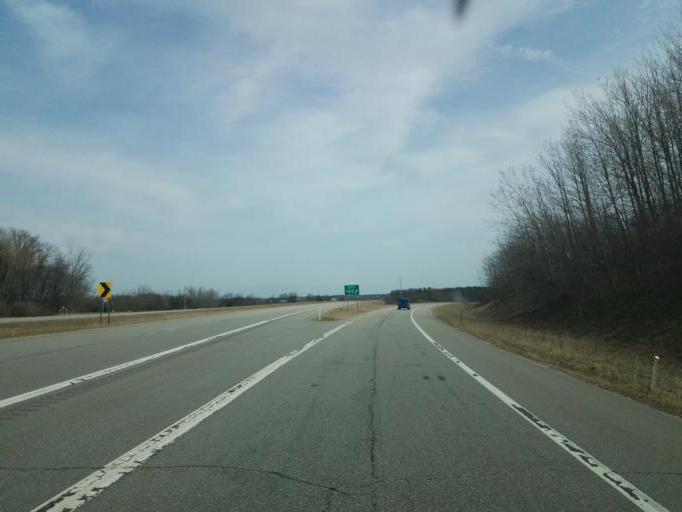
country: US
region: Michigan
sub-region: Mason County
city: Ludington
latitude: 43.9123
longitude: -86.4109
